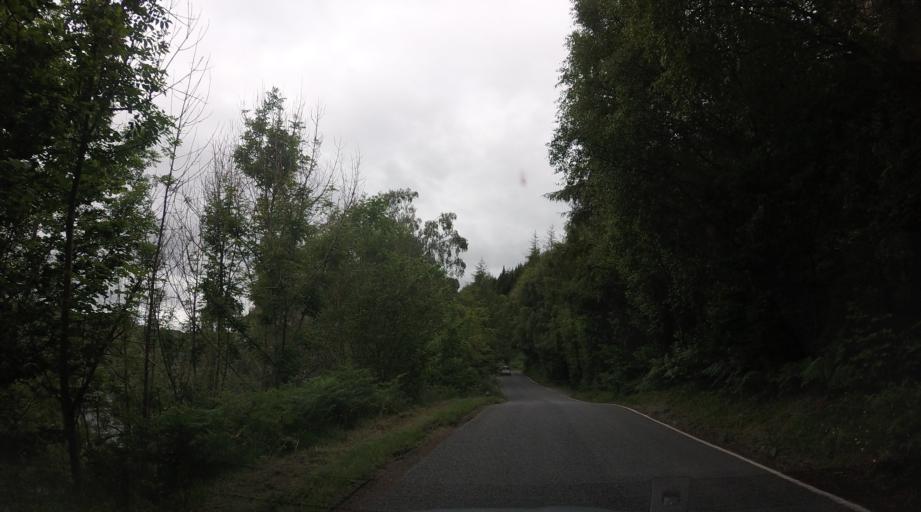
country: GB
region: Scotland
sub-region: Perth and Kinross
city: Aberfeldy
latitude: 56.7201
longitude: -3.8408
